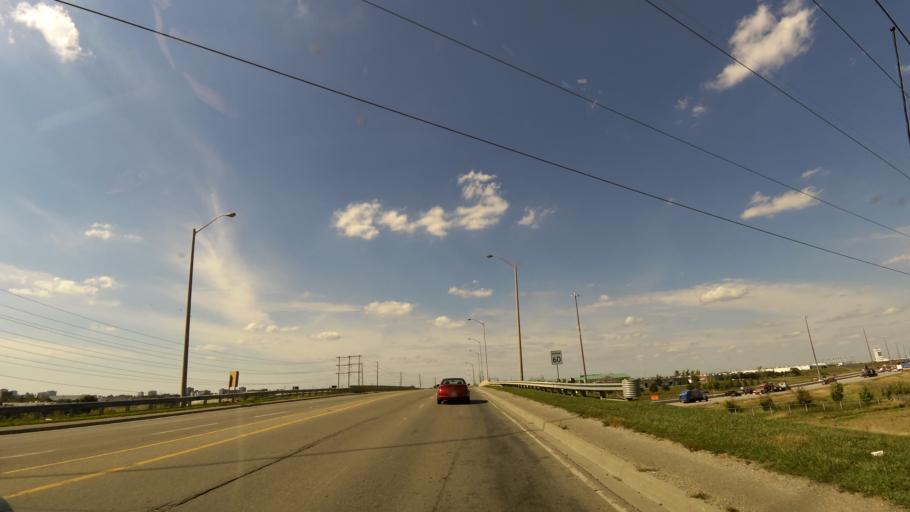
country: CA
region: Ontario
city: Brampton
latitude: 43.7109
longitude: -79.6750
